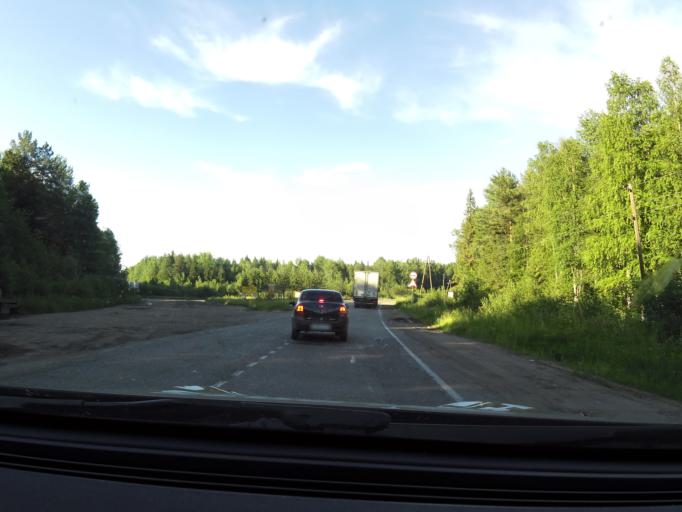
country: RU
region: Kirov
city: Belorechensk
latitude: 58.7988
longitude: 52.4057
